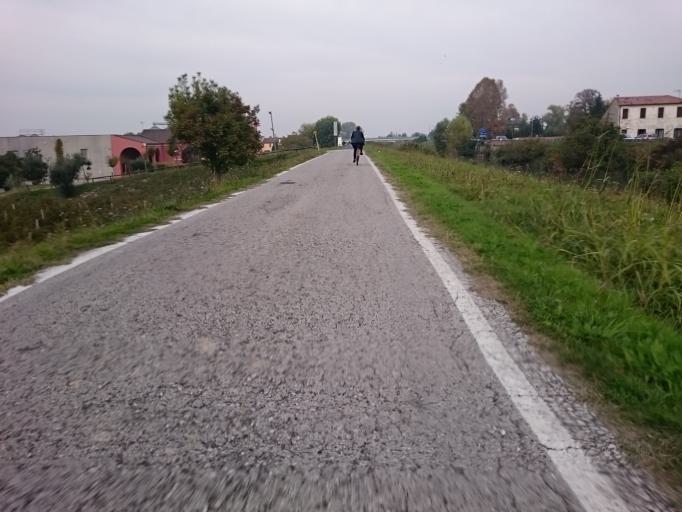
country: IT
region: Veneto
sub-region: Provincia di Padova
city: Montegrotto Terme
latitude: 45.3135
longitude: 11.8021
